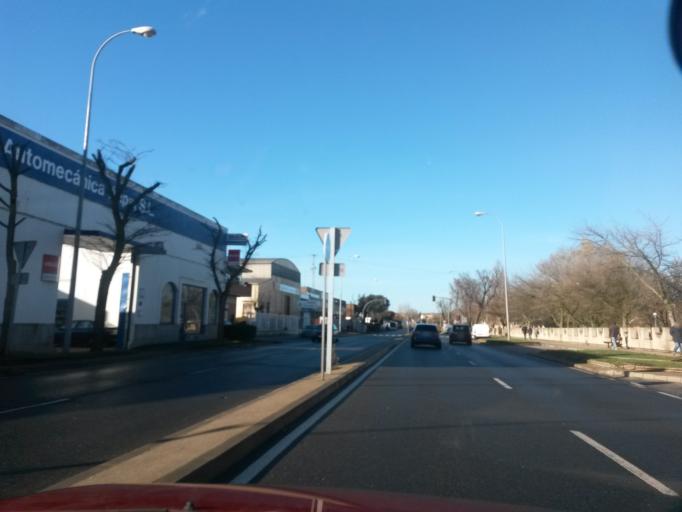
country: ES
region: Castille and Leon
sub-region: Provincia de Salamanca
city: Salamanca
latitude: 40.9549
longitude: -5.6873
